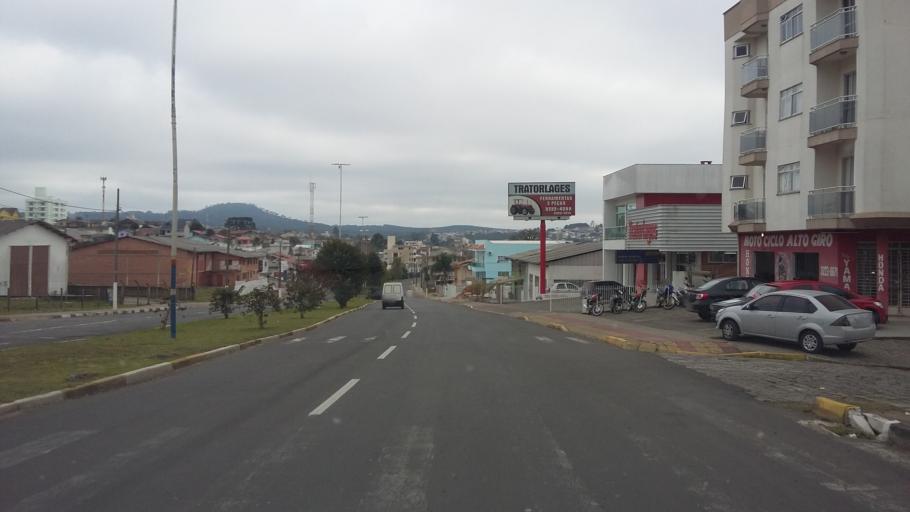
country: BR
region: Santa Catarina
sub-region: Lages
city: Lages
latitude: -27.8265
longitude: -50.3383
